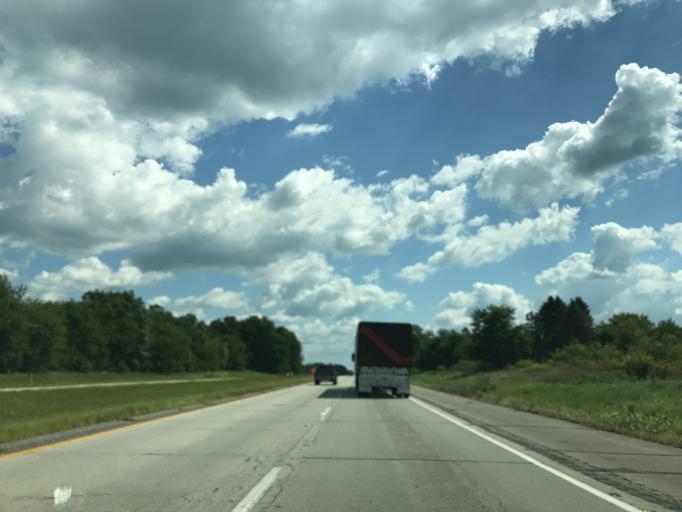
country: US
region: Indiana
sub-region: Starke County
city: Koontz Lake
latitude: 41.3644
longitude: -86.4332
